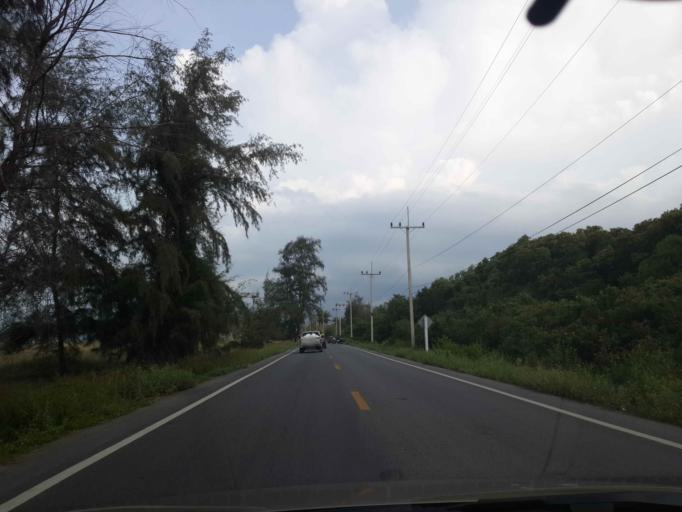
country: TH
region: Pattani
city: Yaring
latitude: 6.9095
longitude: 101.3462
